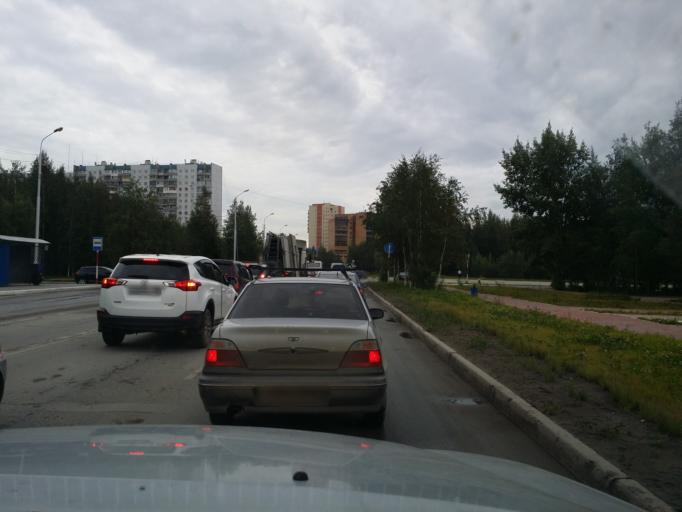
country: RU
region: Khanty-Mansiyskiy Avtonomnyy Okrug
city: Nizhnevartovsk
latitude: 60.9310
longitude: 76.5647
